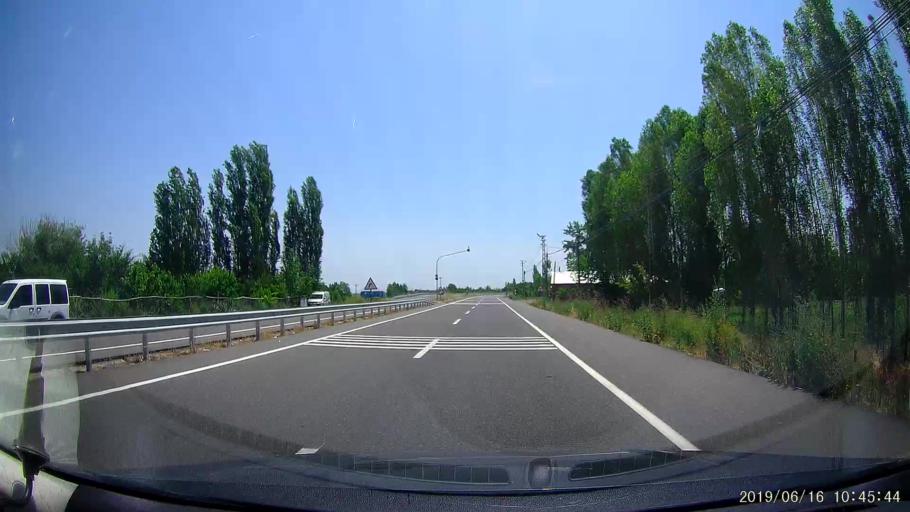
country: AM
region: Armavir
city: Shenavan
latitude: 40.0266
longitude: 43.8726
